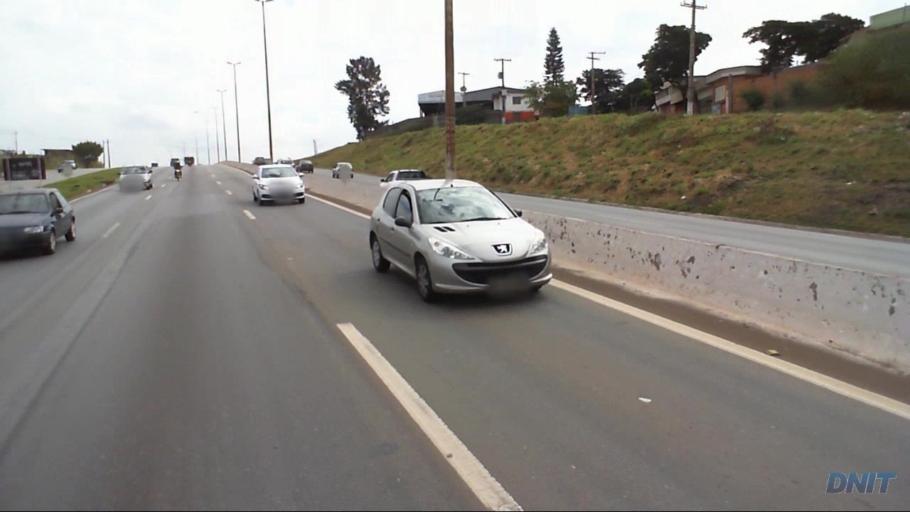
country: BR
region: Minas Gerais
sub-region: Belo Horizonte
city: Belo Horizonte
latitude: -19.8585
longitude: -43.9119
